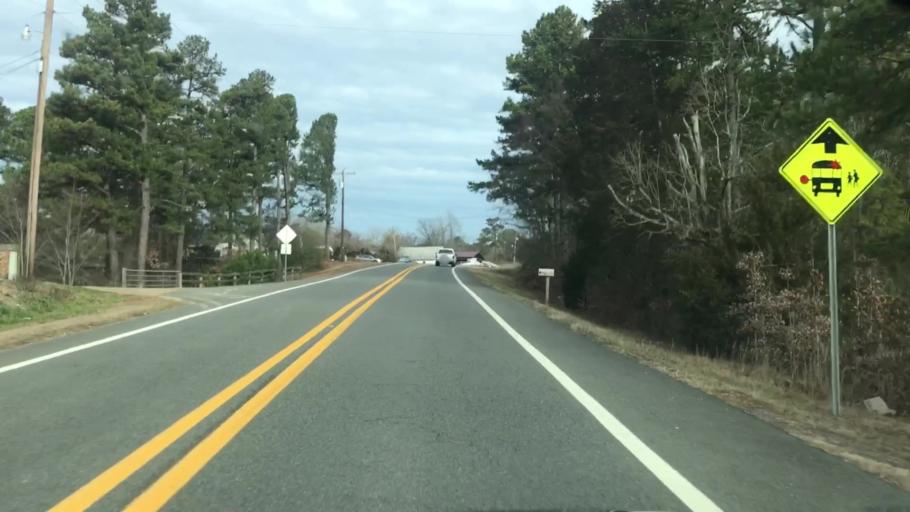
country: US
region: Arkansas
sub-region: Montgomery County
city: Mount Ida
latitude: 34.5837
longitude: -93.6629
